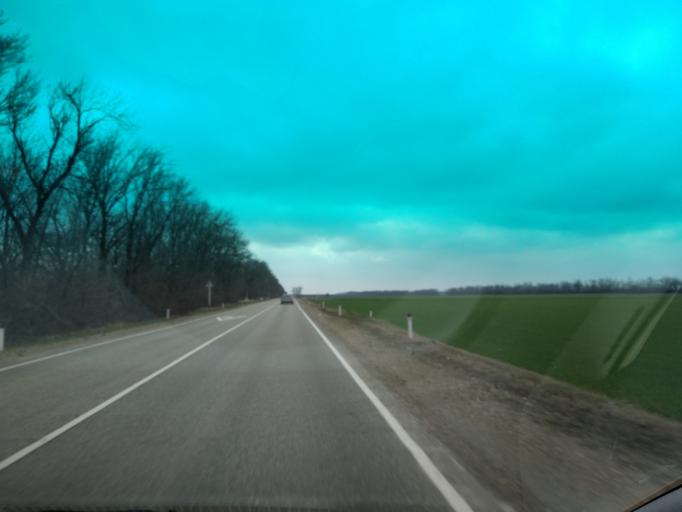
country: RU
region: Krasnodarskiy
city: Novorozhdestvenskaya
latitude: 45.7633
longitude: 39.9300
